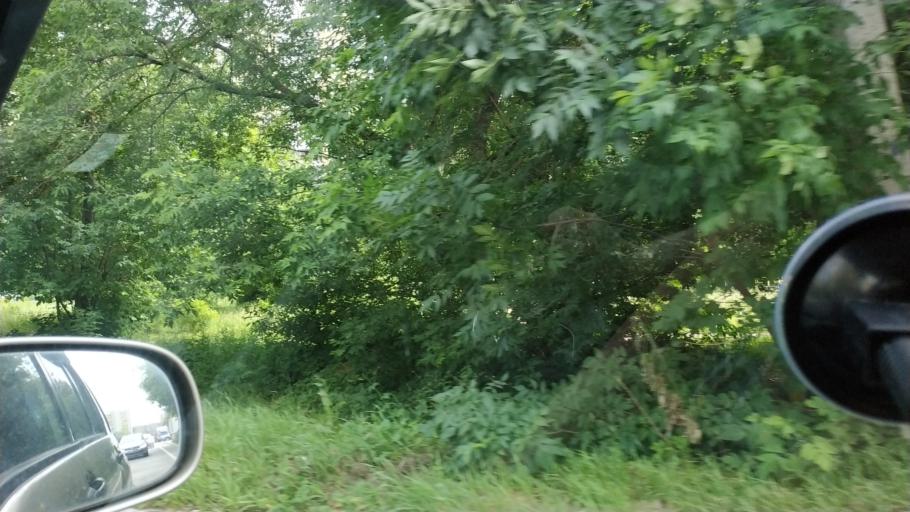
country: RU
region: Moskovskaya
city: Fryazino
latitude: 55.9557
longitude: 38.0612
